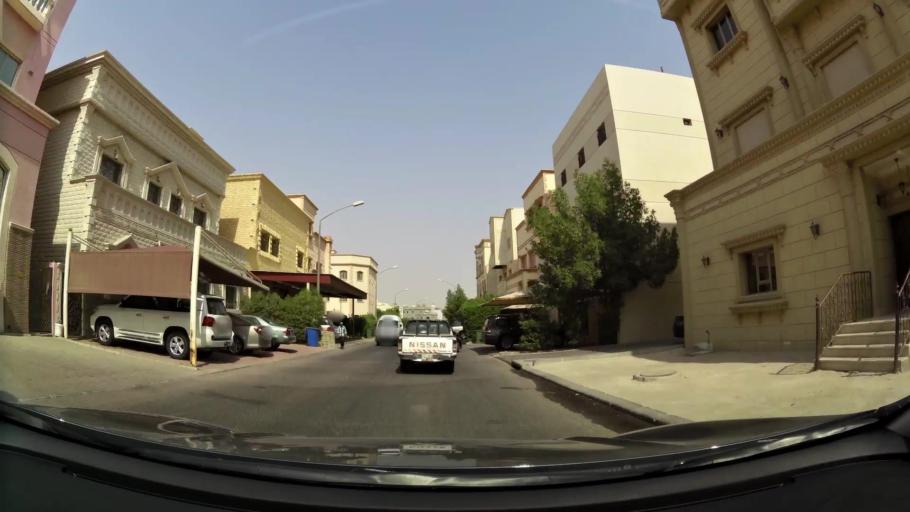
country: KW
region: Muhafazat al Jahra'
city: Al Jahra'
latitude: 29.3057
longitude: 47.7067
